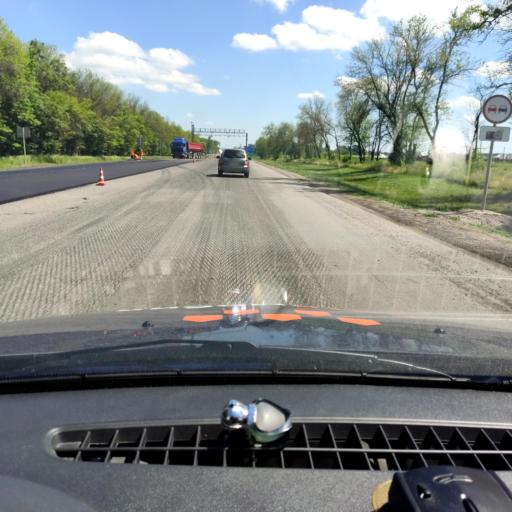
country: RU
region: Orjol
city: Zmiyevka
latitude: 52.7065
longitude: 36.3624
